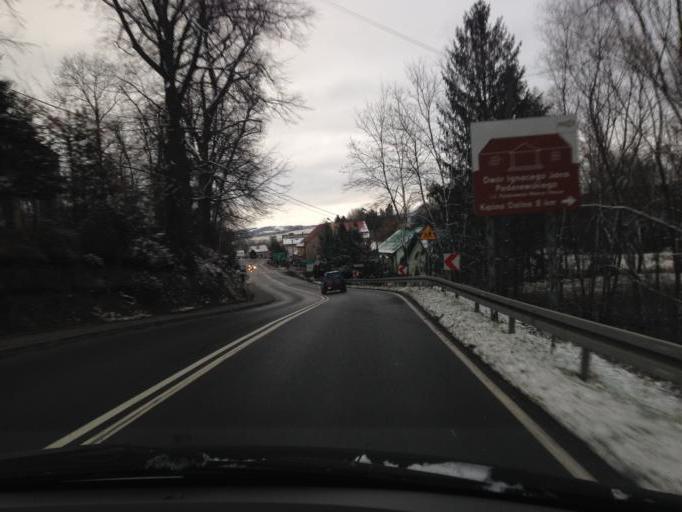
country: PL
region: Lesser Poland Voivodeship
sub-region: Powiat tarnowski
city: Gromnik
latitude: 49.8390
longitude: 20.9569
